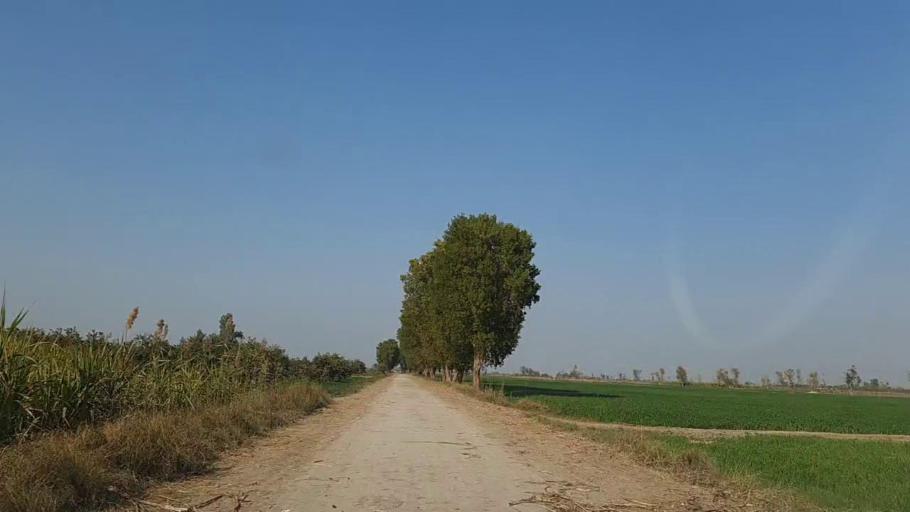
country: PK
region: Sindh
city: Daur
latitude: 26.4814
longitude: 68.2972
